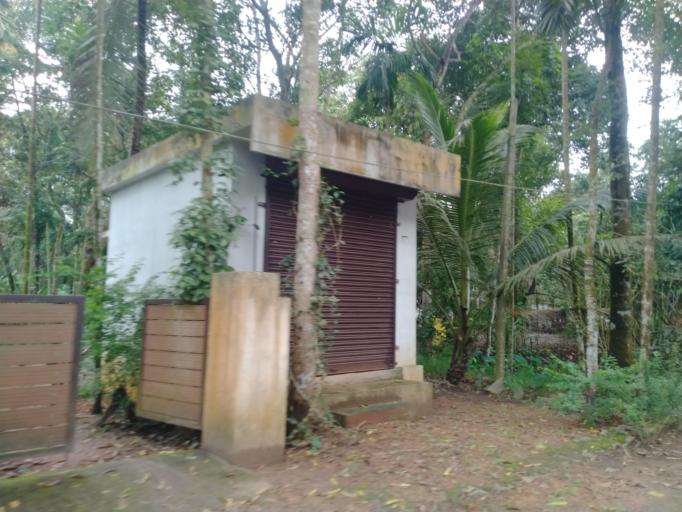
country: IN
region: Kerala
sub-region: Alappuzha
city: Shertallai
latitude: 9.6211
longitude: 76.3564
